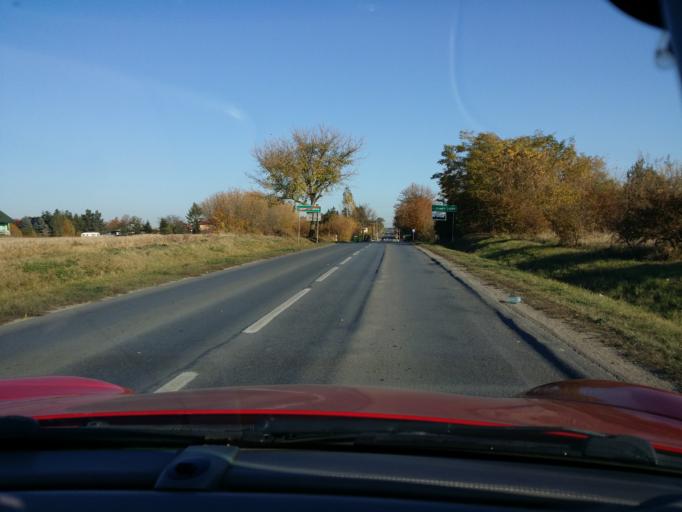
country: PL
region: Masovian Voivodeship
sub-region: Powiat szydlowiecki
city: Jastrzab
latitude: 51.2461
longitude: 20.9741
